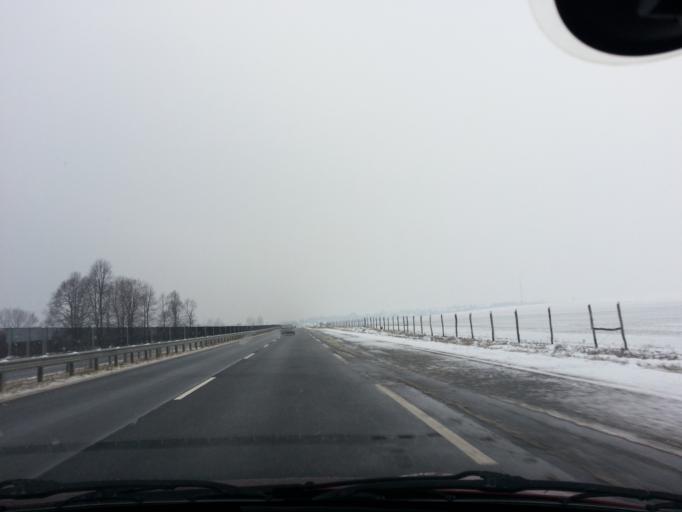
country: HU
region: Nograd
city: Jobbagyi
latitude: 47.8476
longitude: 19.6767
